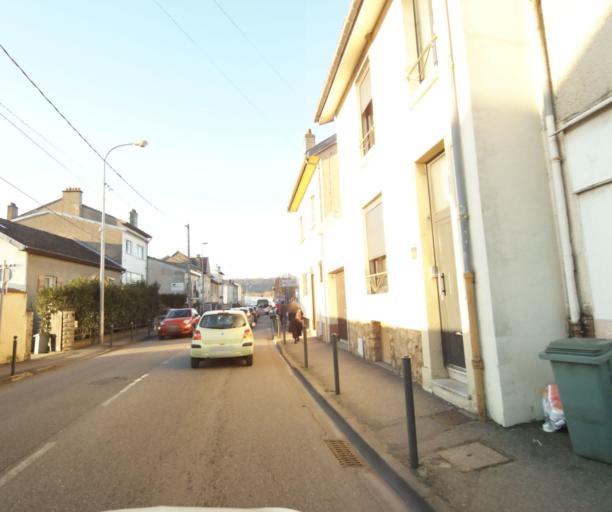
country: FR
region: Lorraine
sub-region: Departement de Meurthe-et-Moselle
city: Maxeville
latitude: 48.7071
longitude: 6.1724
